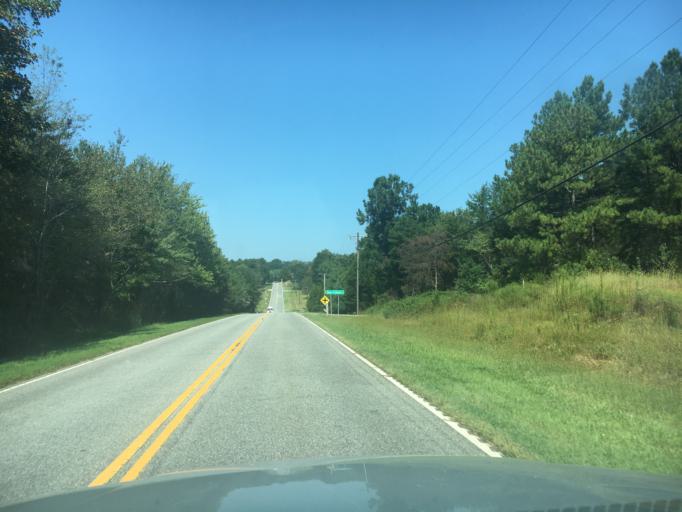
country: US
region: South Carolina
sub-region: Spartanburg County
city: Inman
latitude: 35.1287
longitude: -82.0376
